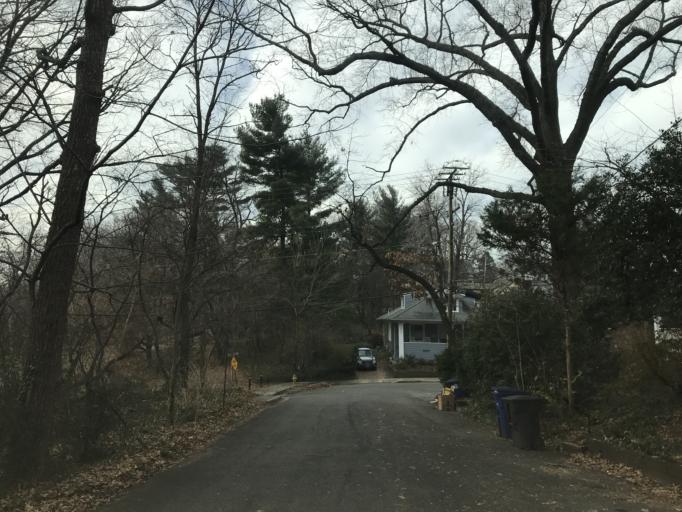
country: US
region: Virginia
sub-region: Arlington County
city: Arlington
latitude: 38.8980
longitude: -77.0963
